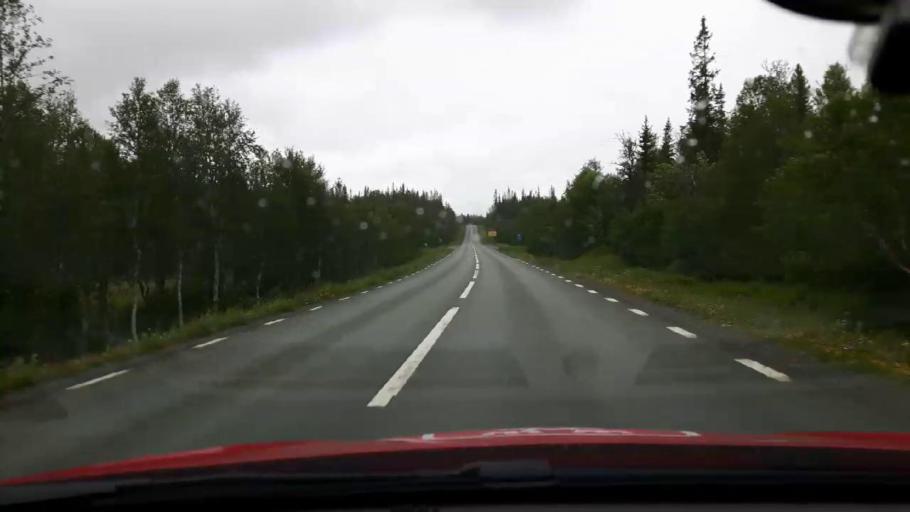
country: NO
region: Nord-Trondelag
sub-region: Meraker
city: Meraker
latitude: 63.3061
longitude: 12.1087
